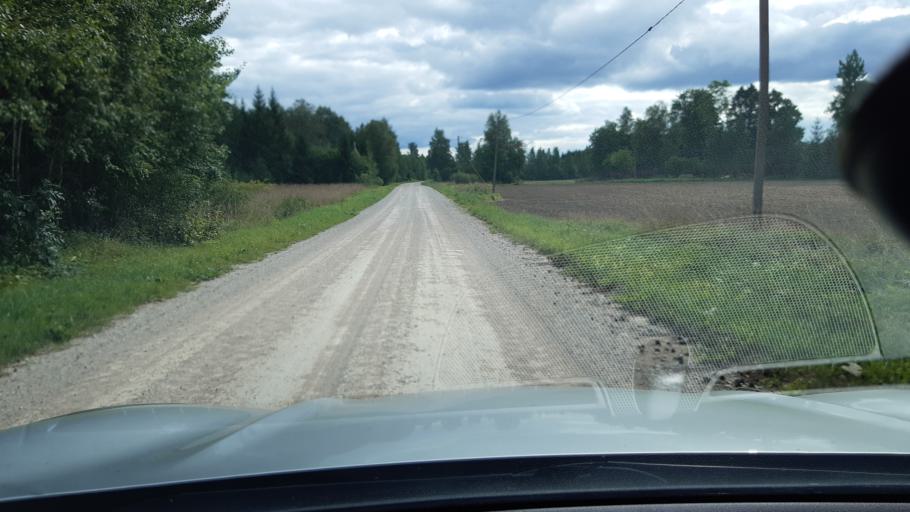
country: EE
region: Paernumaa
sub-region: Vaendra vald (alev)
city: Vandra
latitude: 58.7905
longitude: 25.0164
